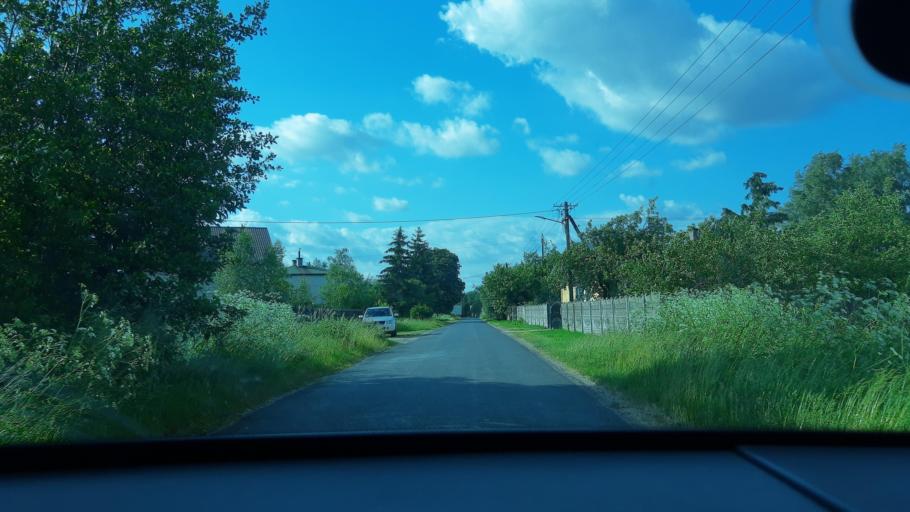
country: PL
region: Lodz Voivodeship
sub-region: Powiat zdunskowolski
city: Zapolice
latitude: 51.5222
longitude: 18.8435
